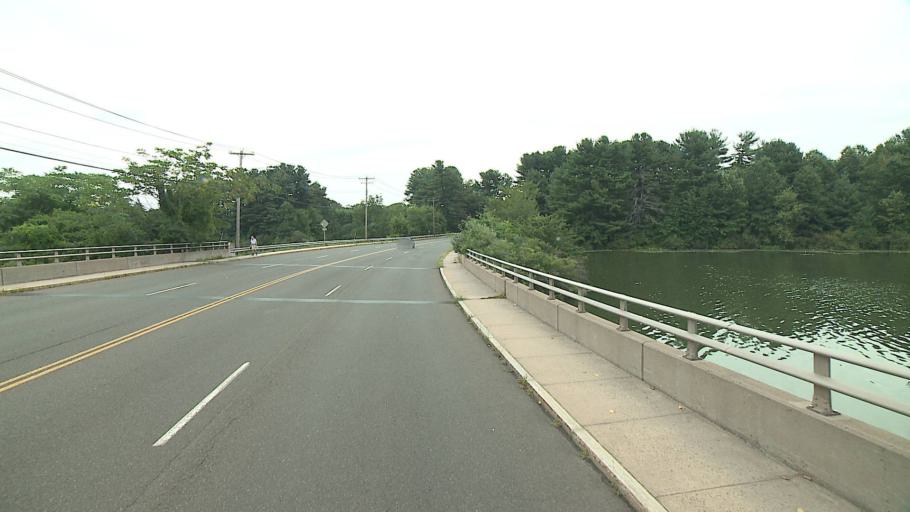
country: US
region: Connecticut
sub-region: New Haven County
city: Hamden
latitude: 41.3542
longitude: -72.9131
